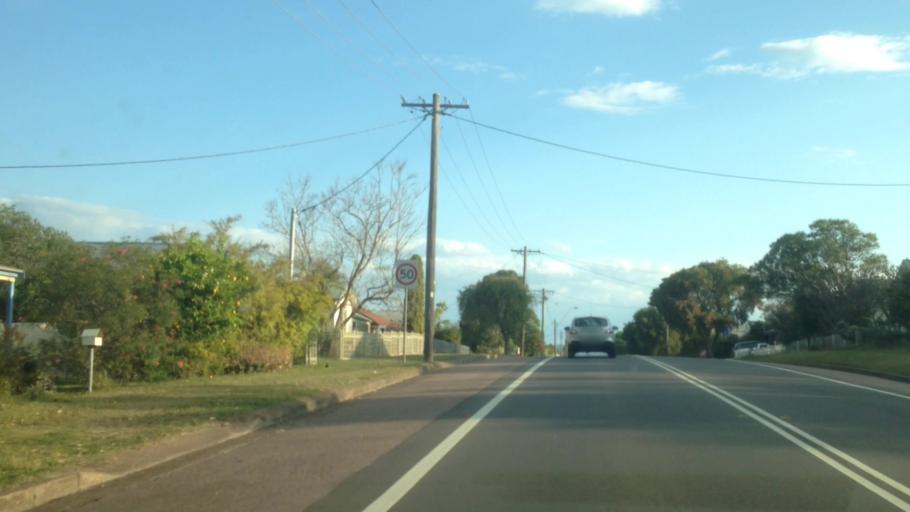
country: AU
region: New South Wales
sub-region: Cessnock
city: Kurri Kurri
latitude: -32.8276
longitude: 151.4817
